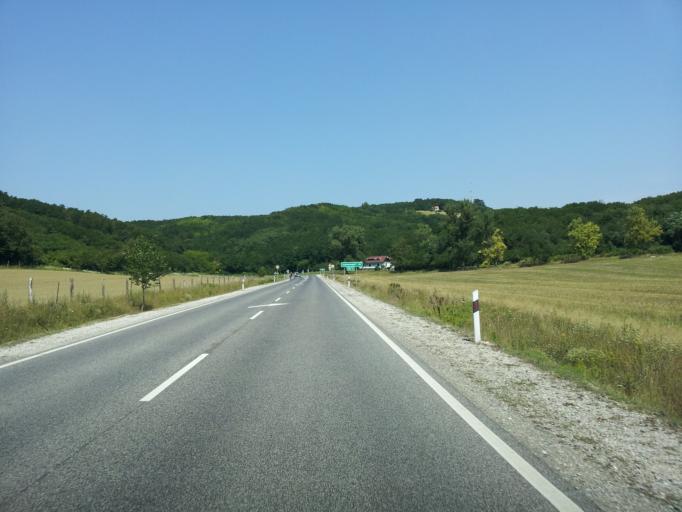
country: HU
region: Zala
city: Zalaegerszeg
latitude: 46.8447
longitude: 16.9241
